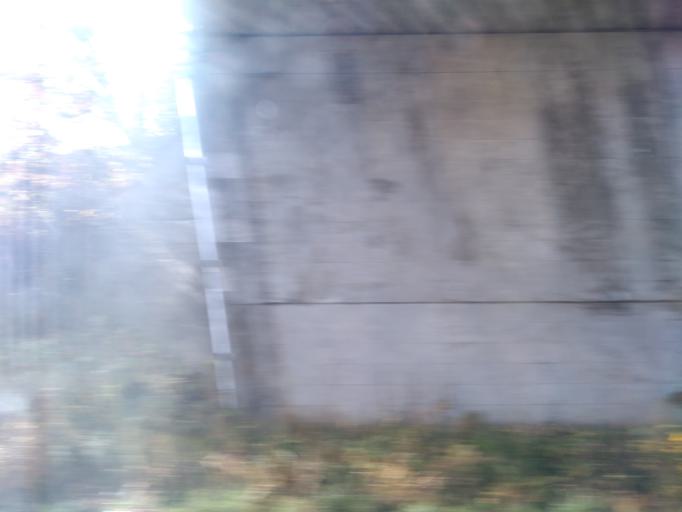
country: JP
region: Hokkaido
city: Kitahiroshima
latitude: 42.9352
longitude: 141.5723
